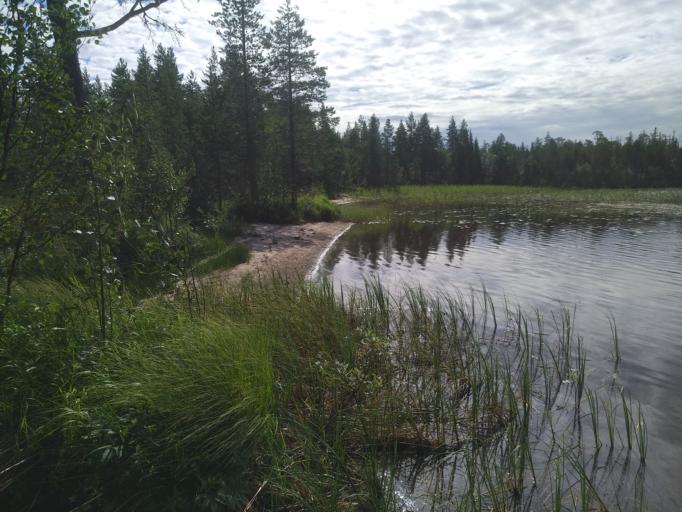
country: RU
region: Republic of Karelia
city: Kalevala
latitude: 64.9853
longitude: 31.2119
